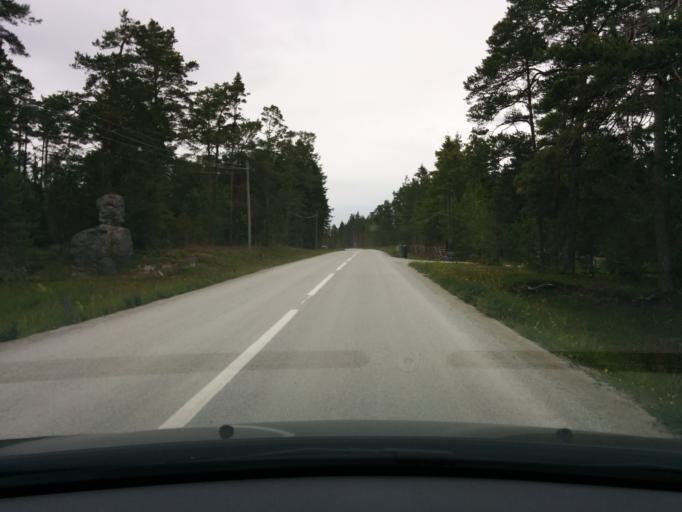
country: SE
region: Gotland
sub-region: Gotland
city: Slite
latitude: 57.6164
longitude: 18.7575
